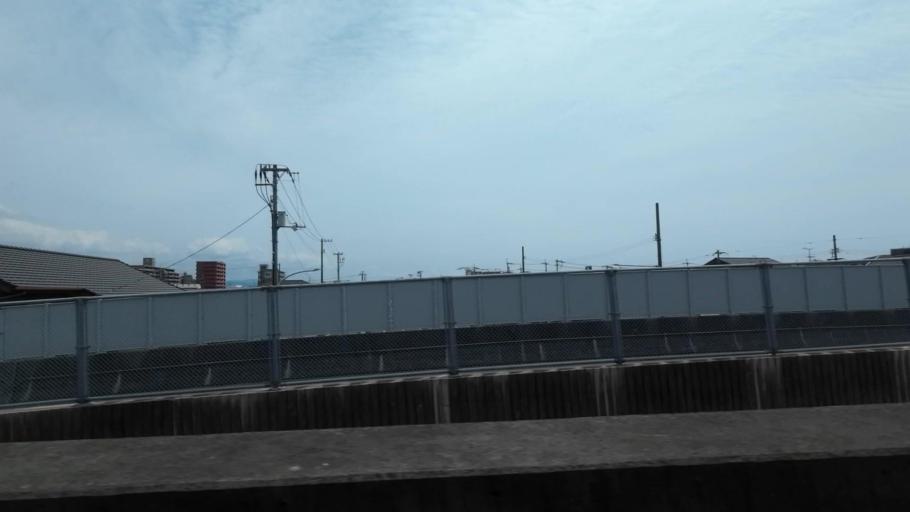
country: JP
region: Kochi
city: Kochi-shi
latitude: 33.5727
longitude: 133.5540
